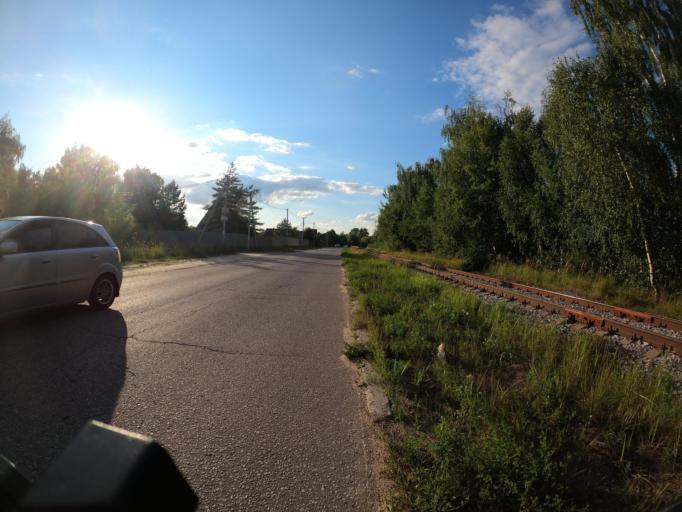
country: RU
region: Moskovskaya
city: Beloozerskiy
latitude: 55.4550
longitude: 38.4852
